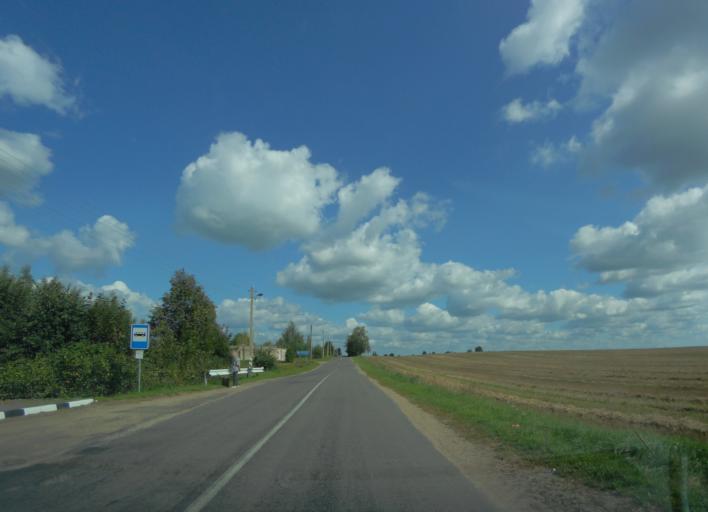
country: BY
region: Minsk
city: Zyembin
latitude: 54.4025
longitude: 28.3967
